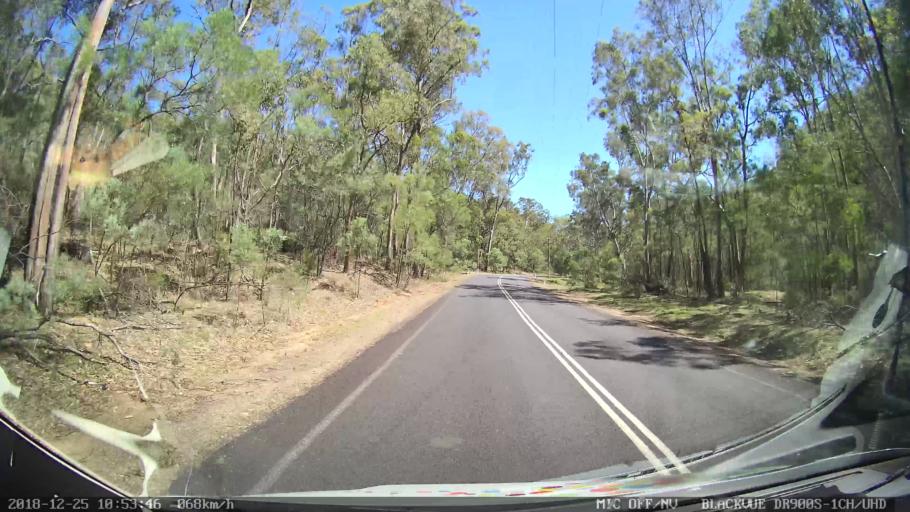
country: AU
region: New South Wales
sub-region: Upper Hunter Shire
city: Merriwa
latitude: -32.4169
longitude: 150.2730
